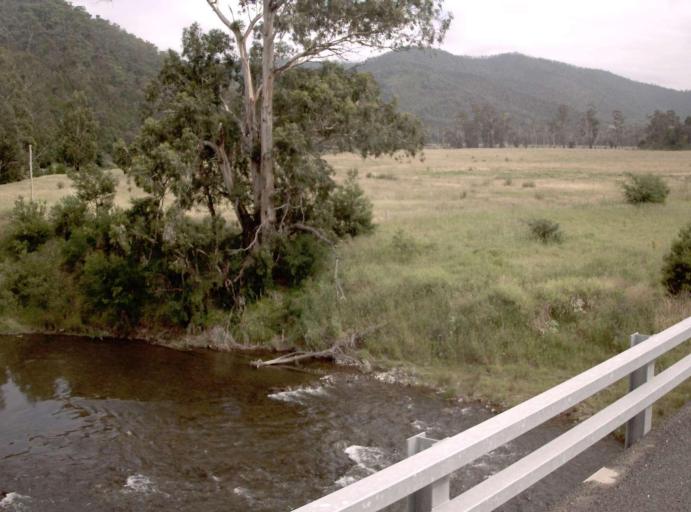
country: AU
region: Victoria
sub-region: Wellington
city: Heyfield
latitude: -37.7621
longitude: 146.6688
